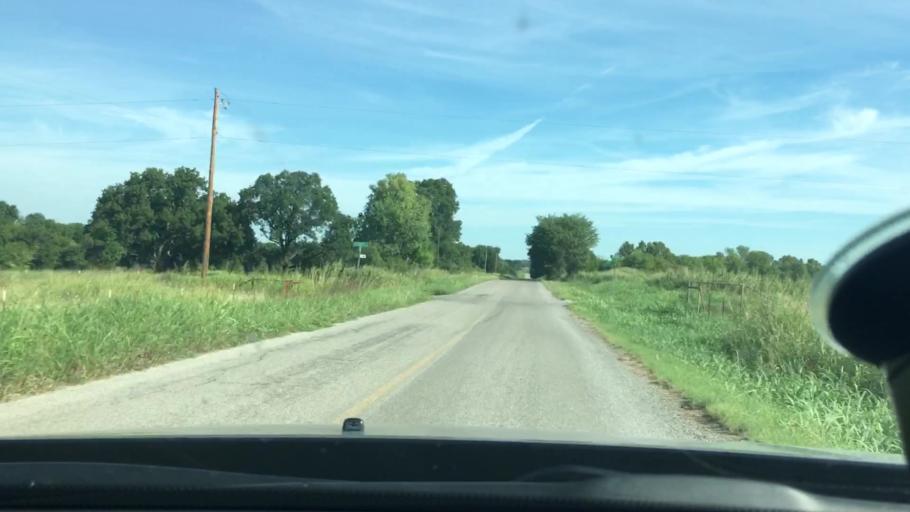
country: US
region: Oklahoma
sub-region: Carter County
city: Lone Grove
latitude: 34.3032
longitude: -97.2824
